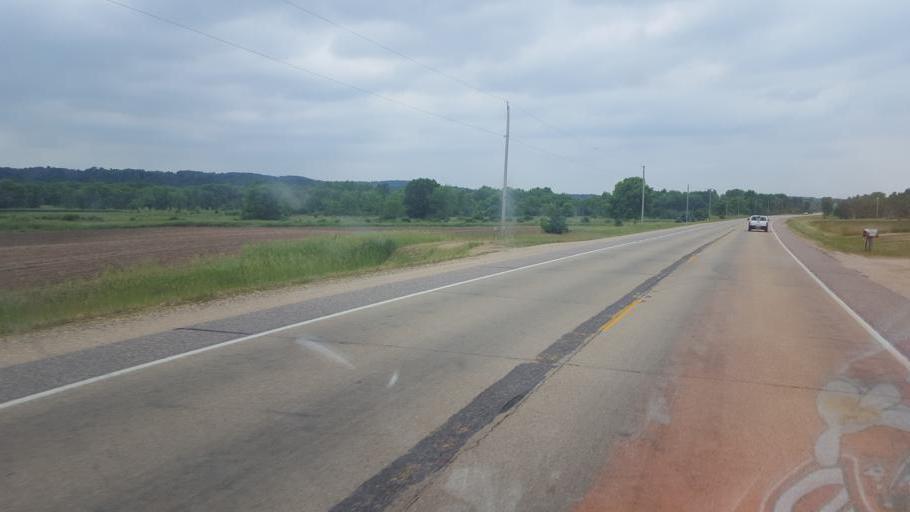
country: US
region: Wisconsin
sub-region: Juneau County
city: Elroy
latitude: 43.6214
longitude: -90.1597
